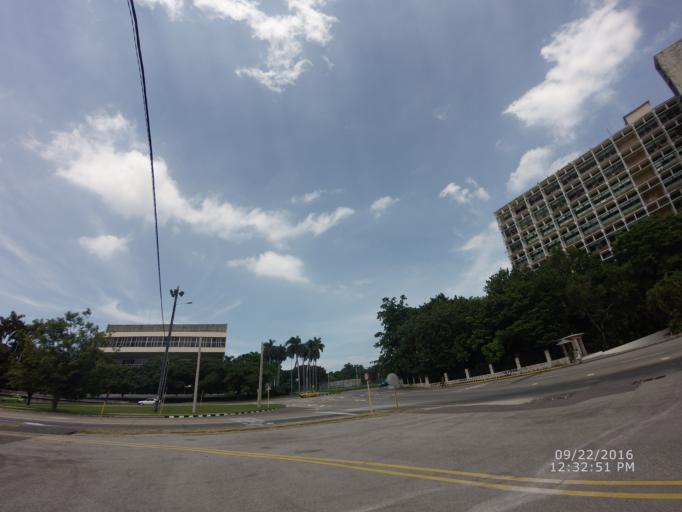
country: CU
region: La Habana
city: Havana
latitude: 23.1252
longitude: -82.3865
